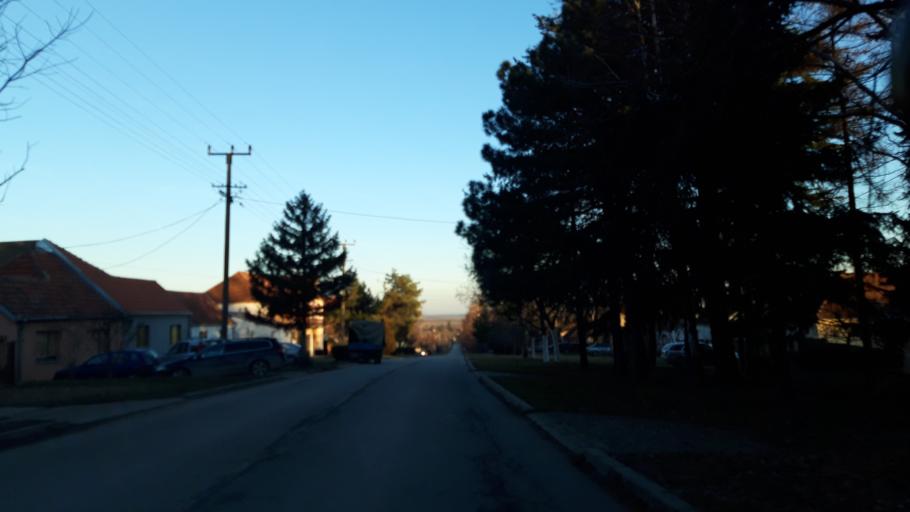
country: RS
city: Cortanovci
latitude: 45.1585
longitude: 20.0085
